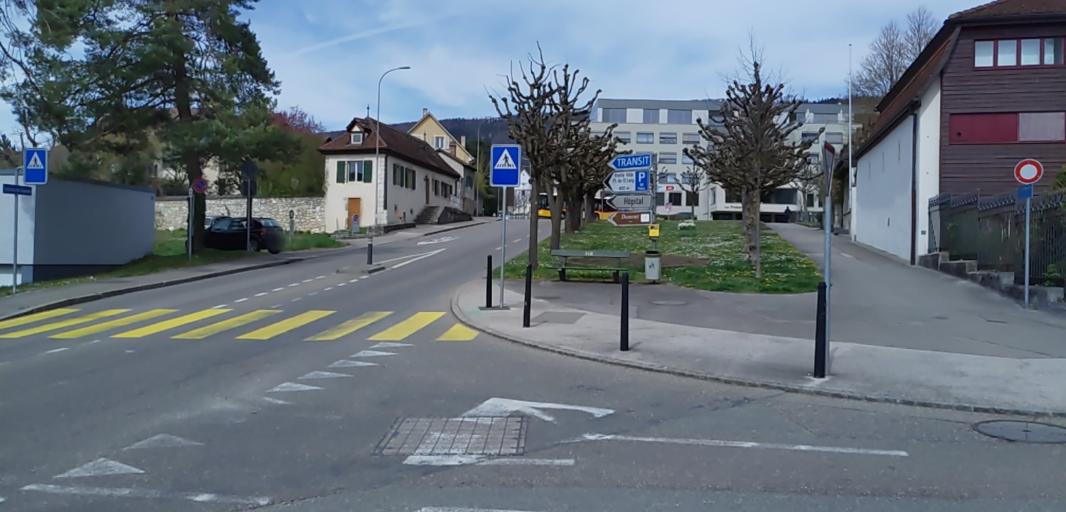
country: CH
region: Jura
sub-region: Delemont District
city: Delemont
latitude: 47.3642
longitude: 7.3417
